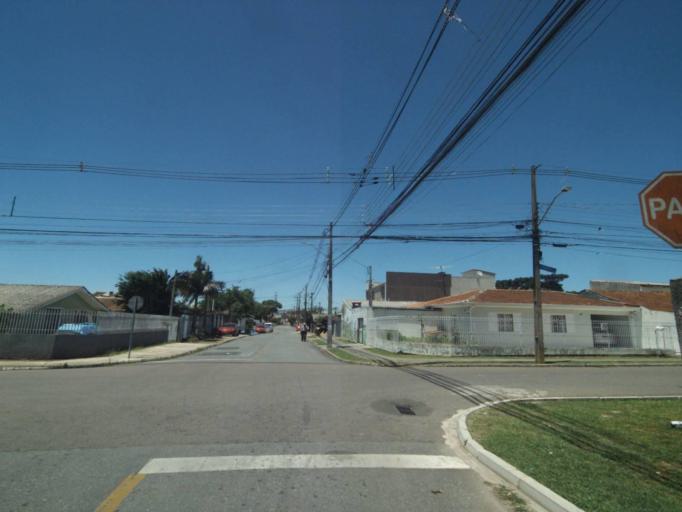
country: BR
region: Parana
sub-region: Curitiba
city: Curitiba
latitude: -25.4747
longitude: -49.3460
